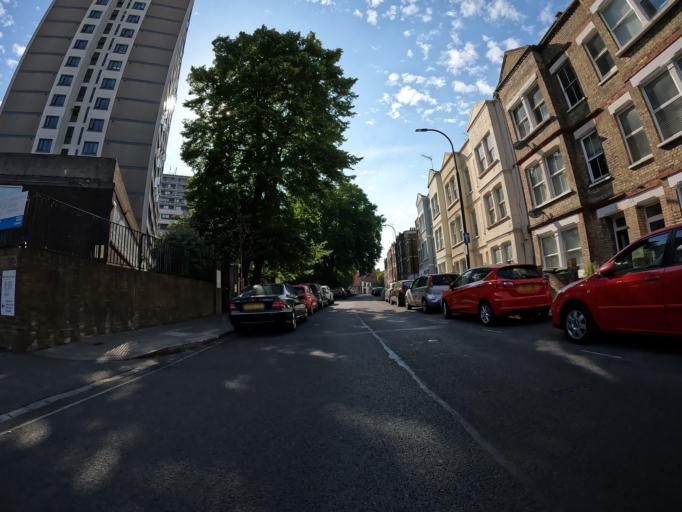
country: GB
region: England
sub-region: Greater London
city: Hendon
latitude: 51.5898
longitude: -0.2219
